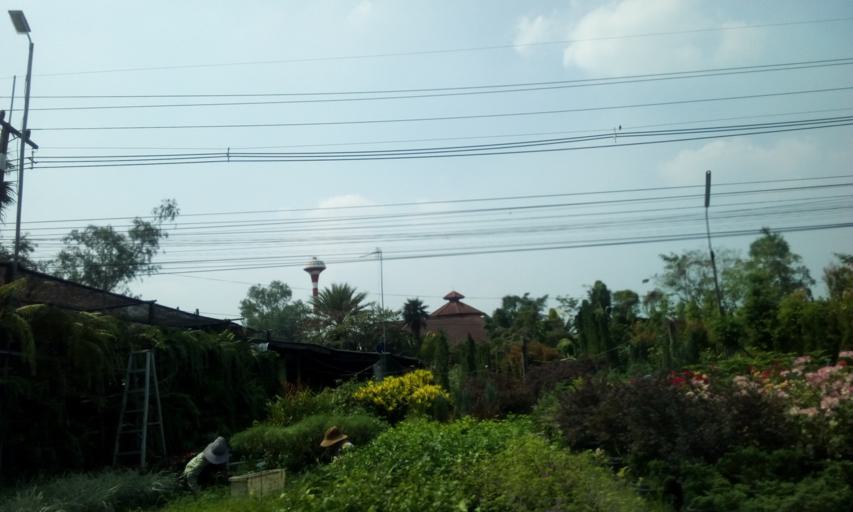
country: TH
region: Nakhon Nayok
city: Ongkharak
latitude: 14.1124
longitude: 100.9434
